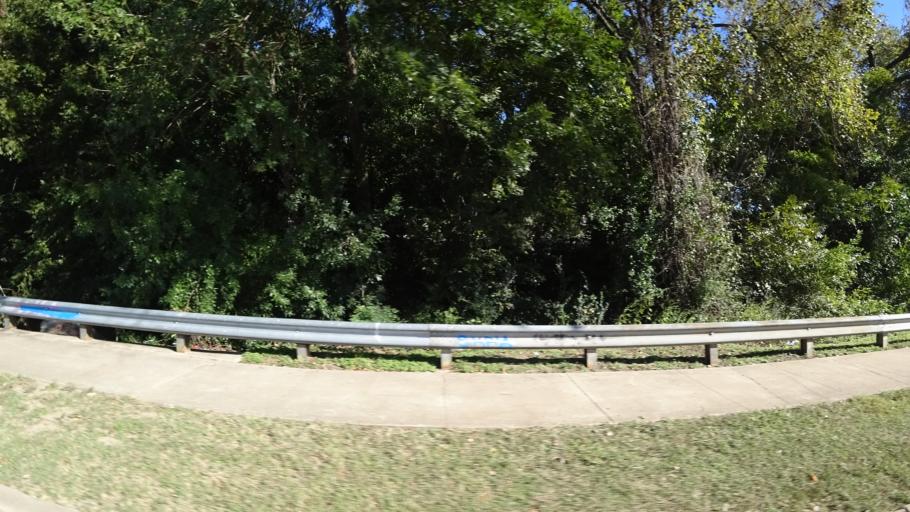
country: US
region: Texas
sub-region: Travis County
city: Austin
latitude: 30.2377
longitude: -97.7384
